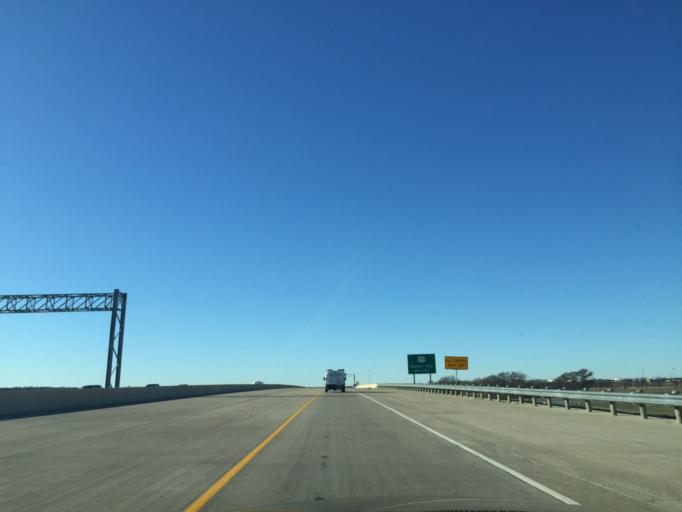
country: US
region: Texas
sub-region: Denton County
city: Roanoke
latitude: 32.9933
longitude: -97.2224
